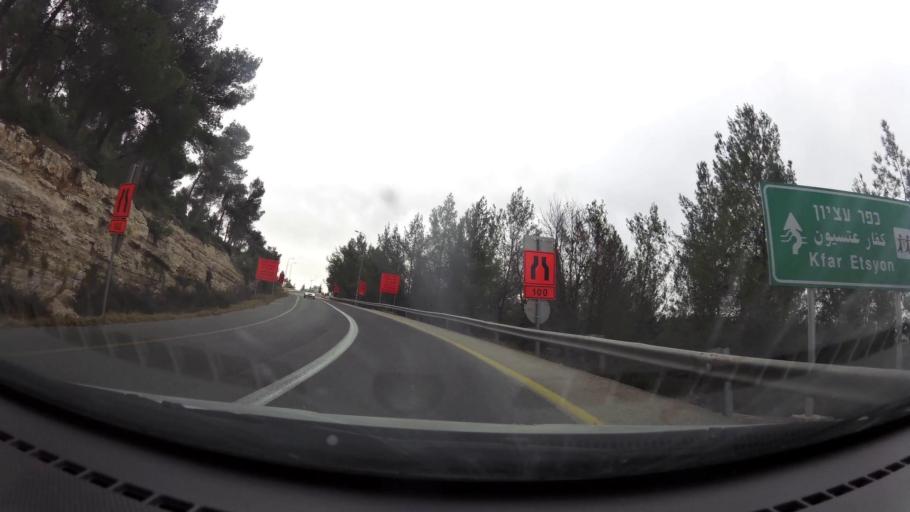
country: PS
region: West Bank
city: Nahhalin
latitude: 31.6575
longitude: 35.1158
